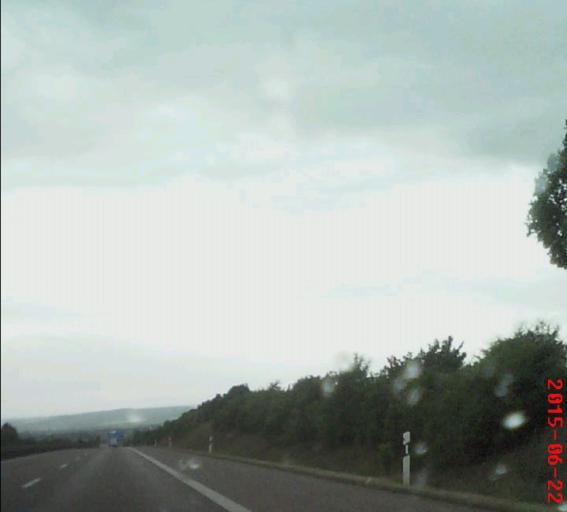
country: DE
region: Saxony-Anhalt
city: Allstedt
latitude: 51.4333
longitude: 11.3674
